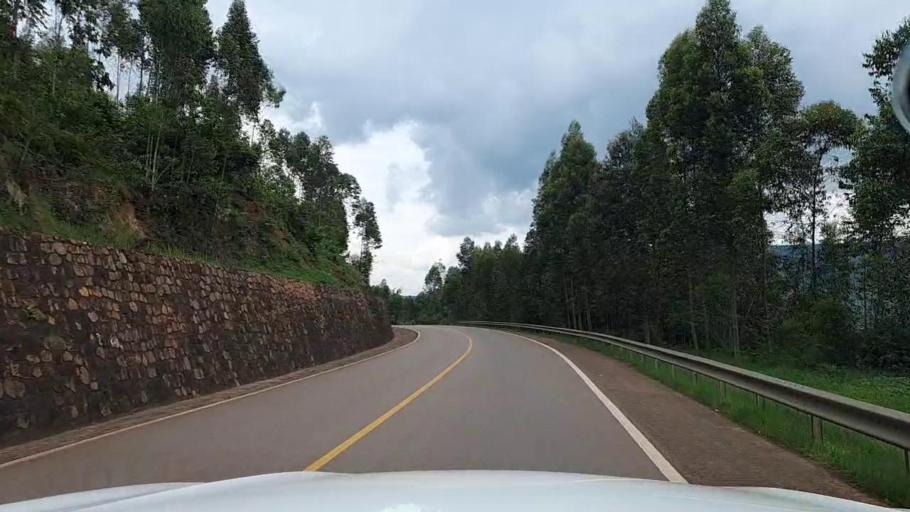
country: RW
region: Kigali
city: Kigali
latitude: -1.7898
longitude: 30.1286
